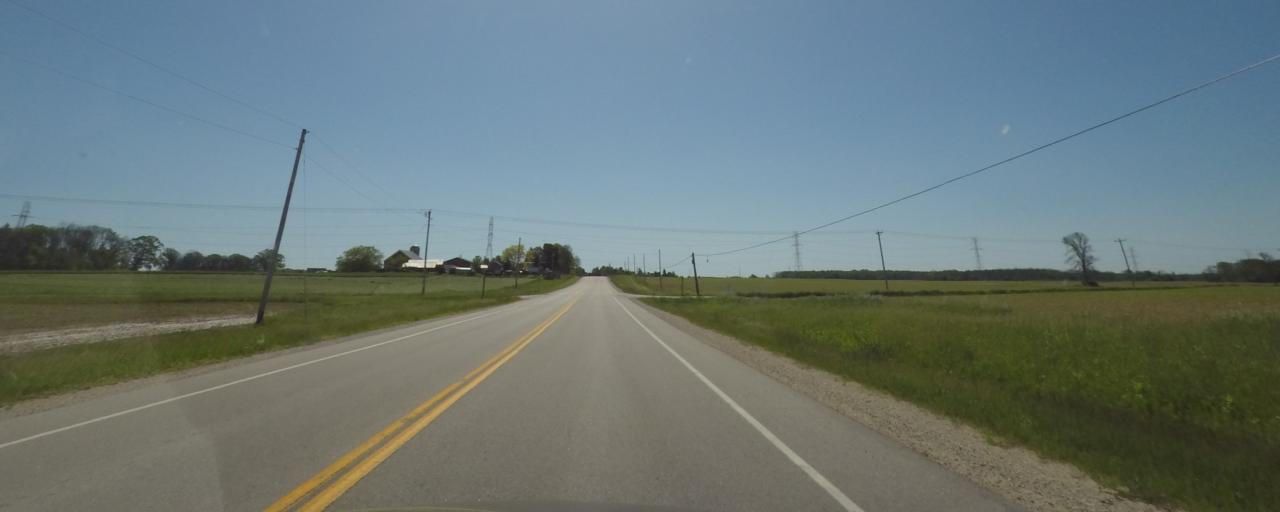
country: US
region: Wisconsin
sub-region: Sheboygan County
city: Sheboygan Falls
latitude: 43.7455
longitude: -87.8815
